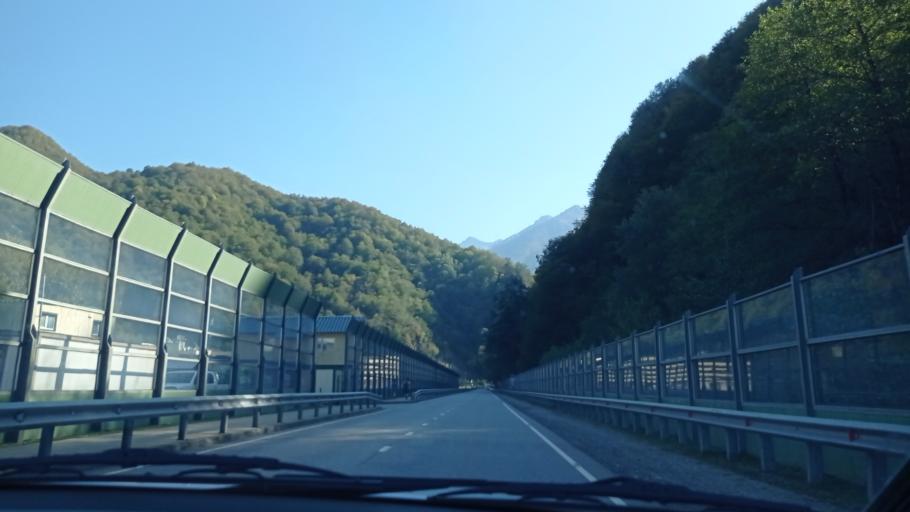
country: RU
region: Krasnodarskiy
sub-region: Sochi City
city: Krasnaya Polyana
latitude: 43.6864
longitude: 40.2761
